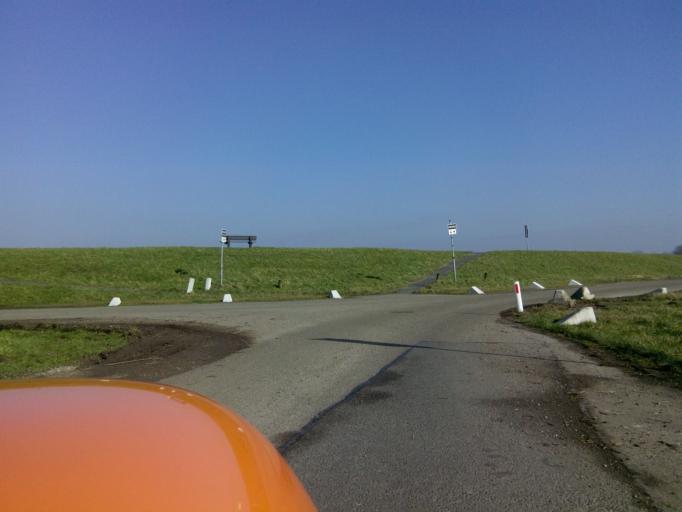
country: NL
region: Gelderland
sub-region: Gemeente Nijkerk
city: Nijkerk
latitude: 52.2528
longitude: 5.4559
